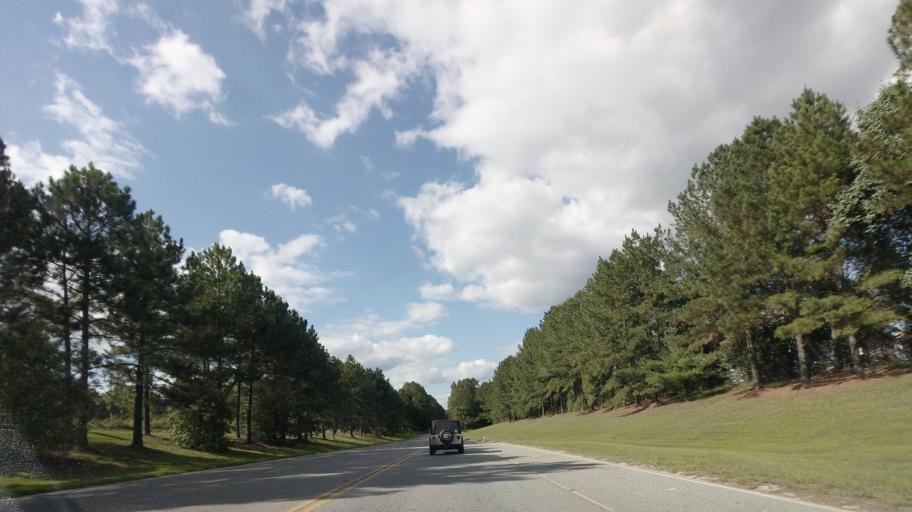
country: US
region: Georgia
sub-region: Bibb County
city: Macon
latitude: 32.9981
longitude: -83.7368
